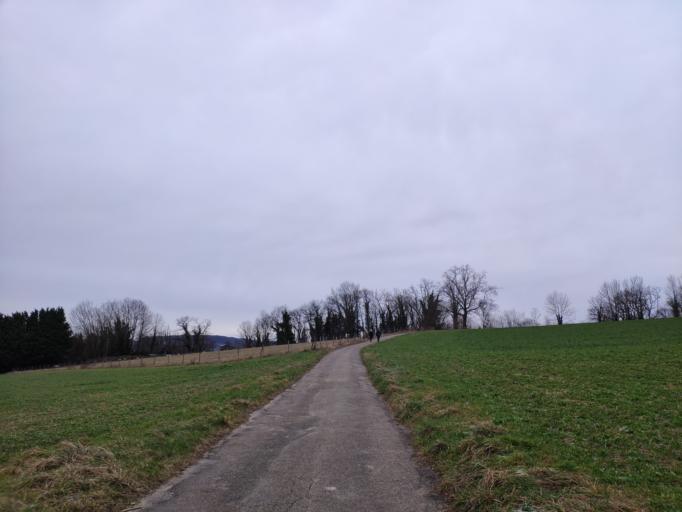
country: CH
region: Basel-City
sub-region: Basel-Stadt
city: Bettingen
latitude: 47.5857
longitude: 7.6691
